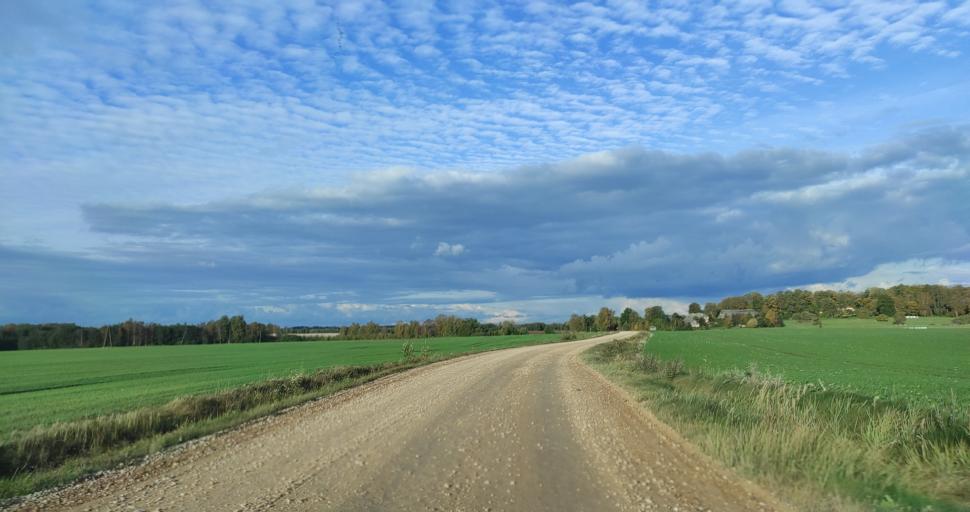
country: LV
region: Aizpute
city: Aizpute
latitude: 56.7476
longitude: 21.8066
